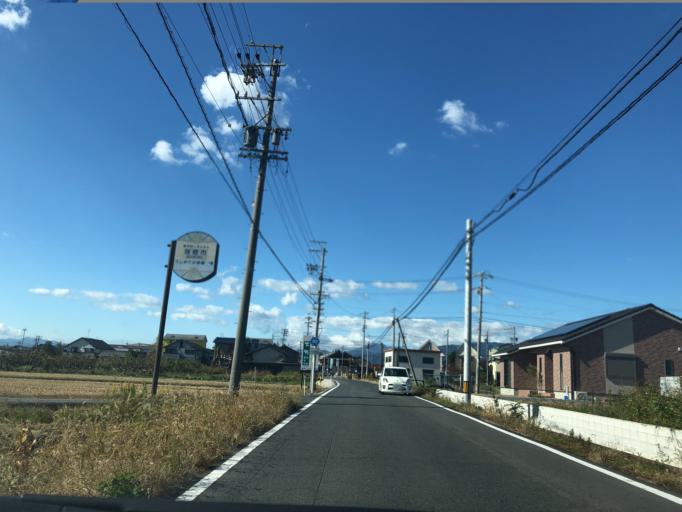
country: JP
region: Gifu
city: Godo
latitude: 35.4120
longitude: 136.6624
